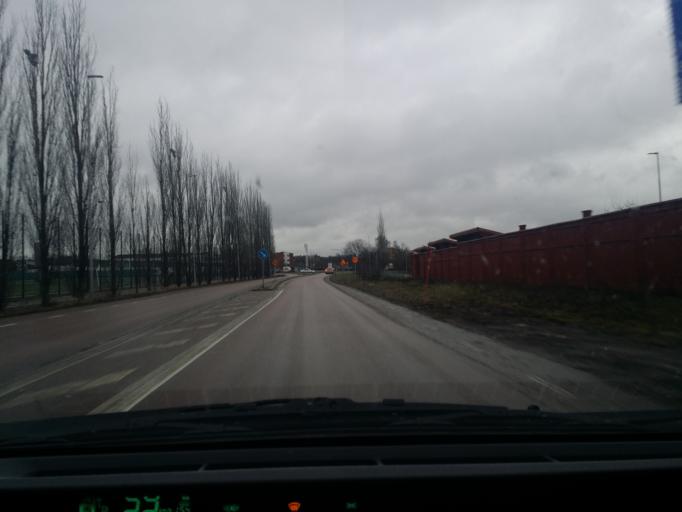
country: SE
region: Vaestmanland
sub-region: Sala Kommun
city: Sala
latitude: 59.9202
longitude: 16.5872
